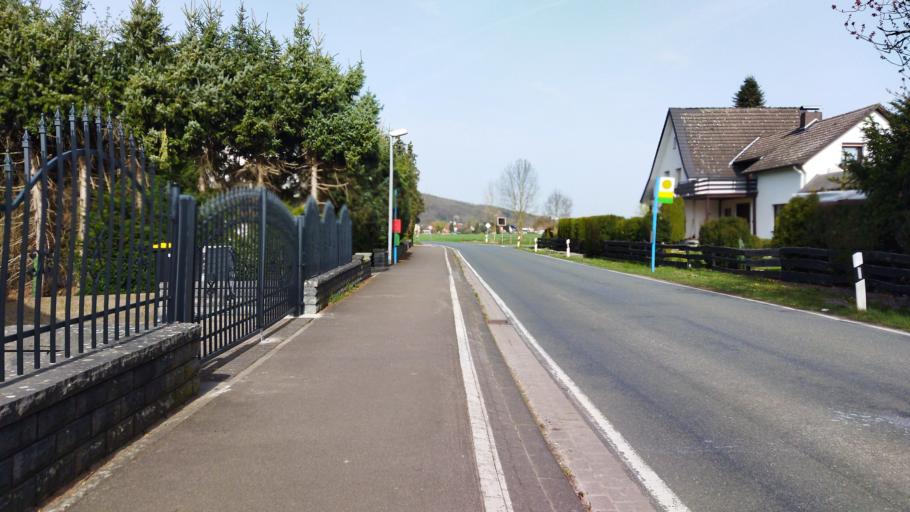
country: DE
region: North Rhine-Westphalia
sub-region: Regierungsbezirk Detmold
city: Vlotho
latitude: 52.1680
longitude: 8.8796
